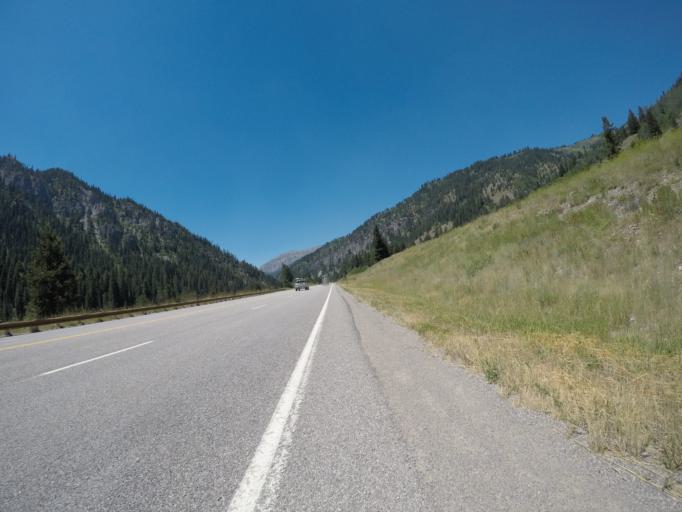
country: US
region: Wyoming
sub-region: Teton County
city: Hoback
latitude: 43.1974
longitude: -110.8921
